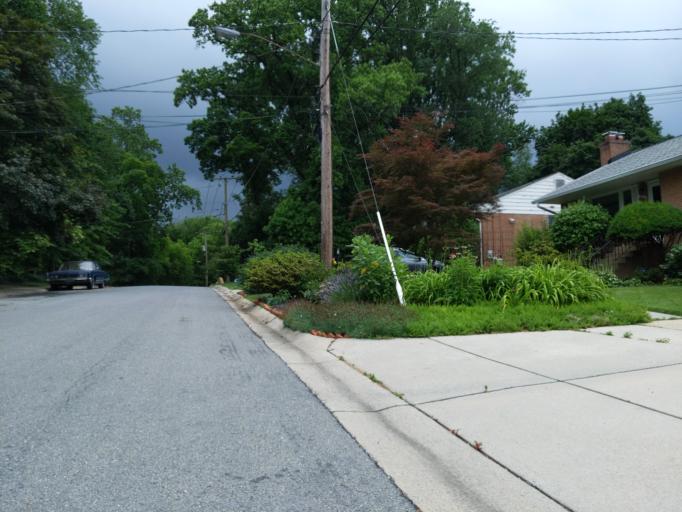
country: US
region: Maryland
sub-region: Montgomery County
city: Forest Glen
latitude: 39.0043
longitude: -77.0458
